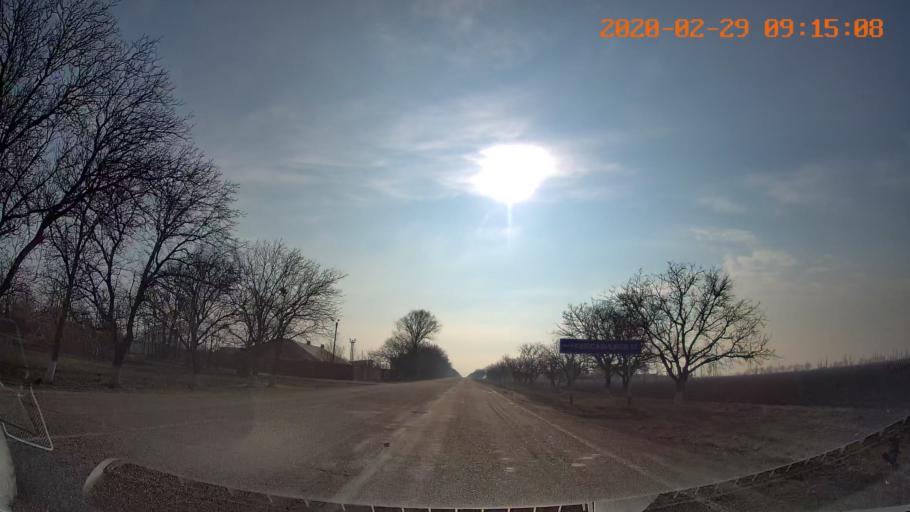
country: MD
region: Telenesti
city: Pervomaisc
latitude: 46.8031
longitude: 29.8640
